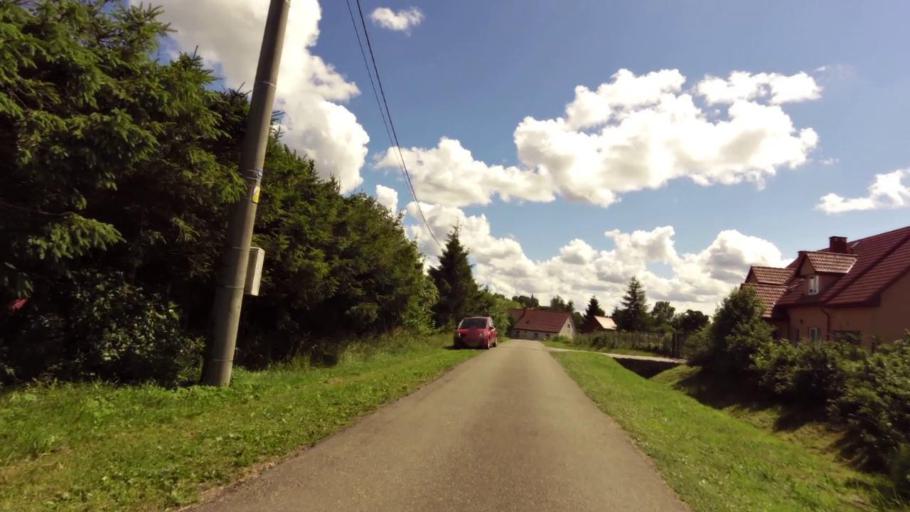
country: PL
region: West Pomeranian Voivodeship
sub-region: Powiat slawienski
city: Slawno
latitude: 54.5247
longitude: 16.6078
